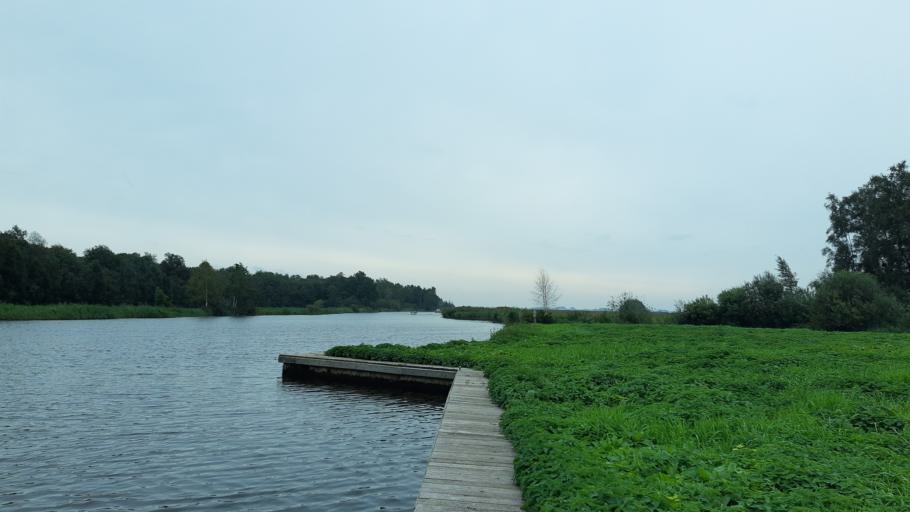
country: NL
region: Overijssel
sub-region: Gemeente Steenwijkerland
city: Sint Jansklooster
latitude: 52.7111
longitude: 6.0218
